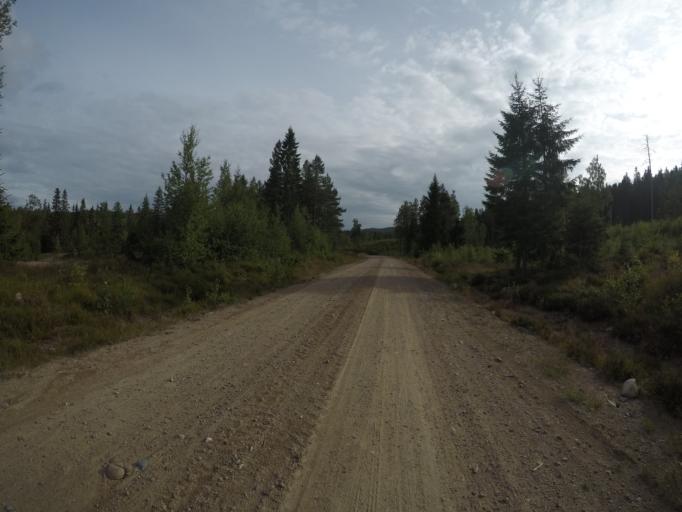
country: SE
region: Vaermland
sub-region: Filipstads Kommun
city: Lesjofors
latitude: 60.1990
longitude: 14.3179
